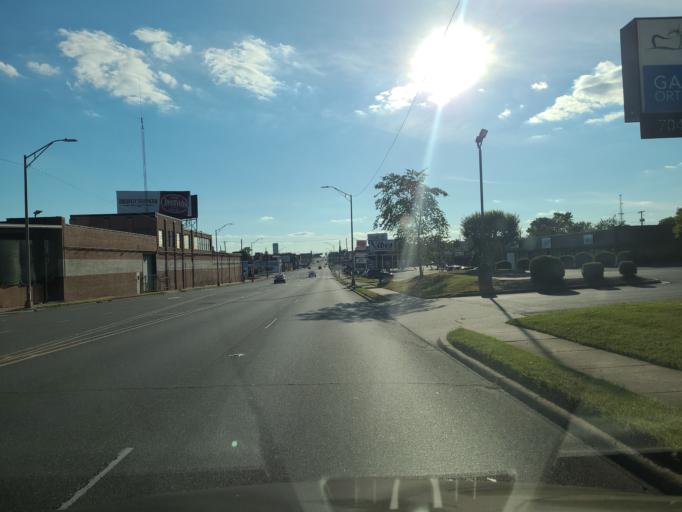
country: US
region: North Carolina
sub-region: Gaston County
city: Gastonia
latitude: 35.2624
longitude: -81.1687
